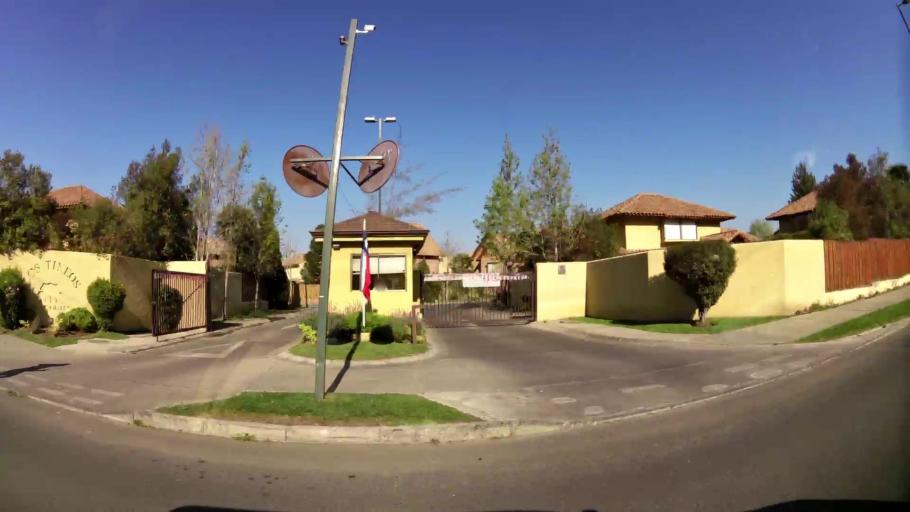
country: CL
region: Santiago Metropolitan
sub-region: Provincia de Chacabuco
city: Chicureo Abajo
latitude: -33.3518
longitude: -70.6643
